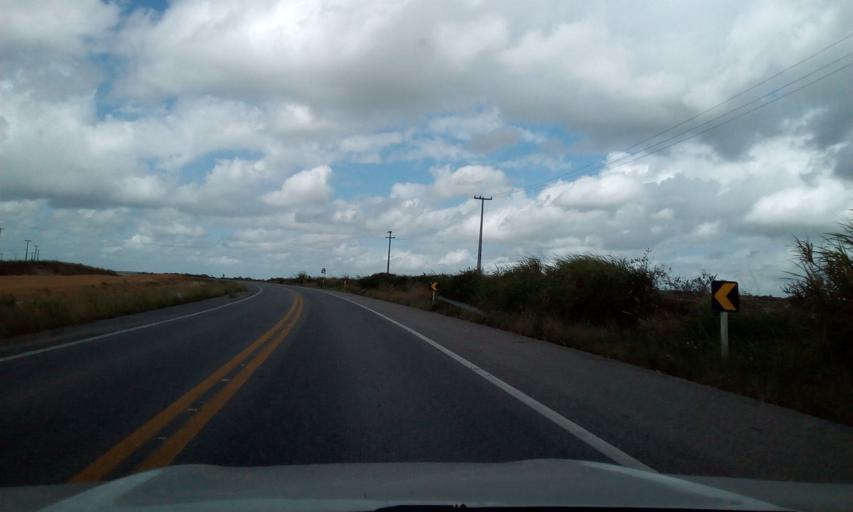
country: BR
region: Alagoas
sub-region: Pilar
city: Pilar
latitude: -9.5850
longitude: -35.9755
